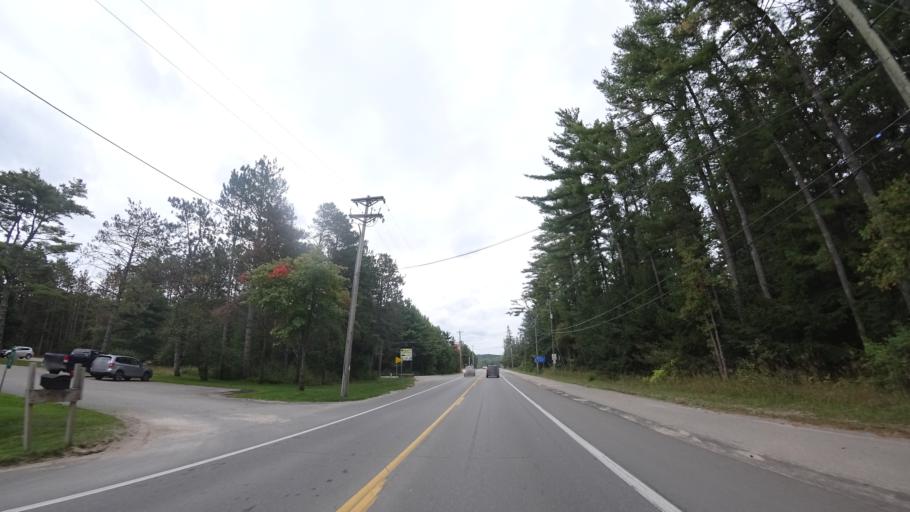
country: US
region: Michigan
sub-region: Emmet County
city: Petoskey
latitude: 45.4240
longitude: -84.9045
